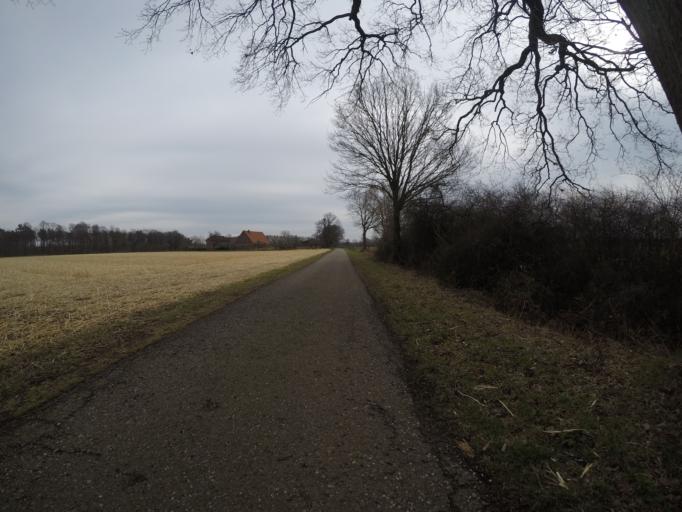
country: DE
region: North Rhine-Westphalia
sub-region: Regierungsbezirk Dusseldorf
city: Hamminkeln
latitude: 51.7545
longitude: 6.6021
